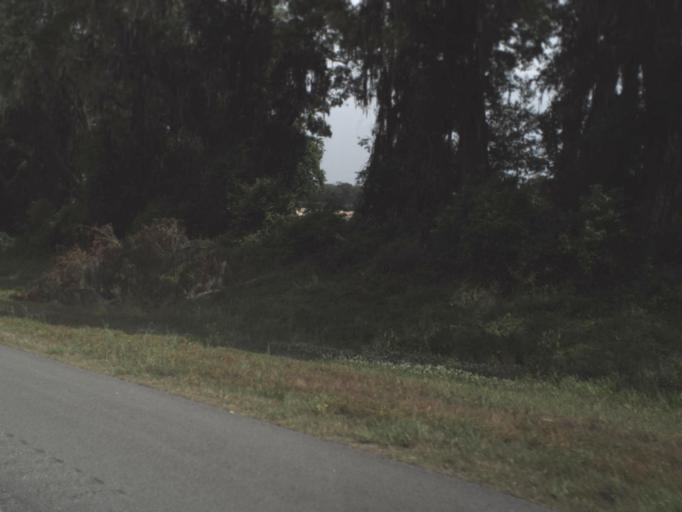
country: US
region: Florida
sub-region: Suwannee County
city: Live Oak
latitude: 30.3523
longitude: -83.0341
